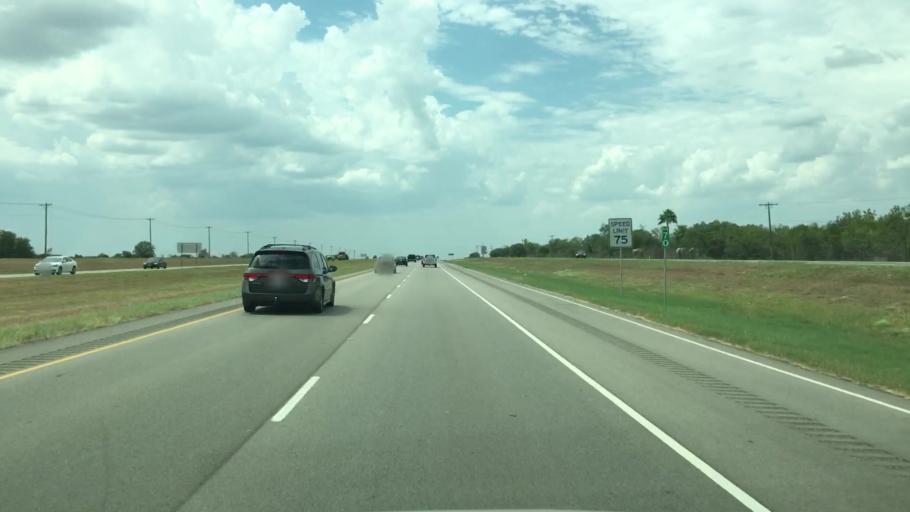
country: US
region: Texas
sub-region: Live Oak County
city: Three Rivers
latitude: 28.4974
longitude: -98.1518
